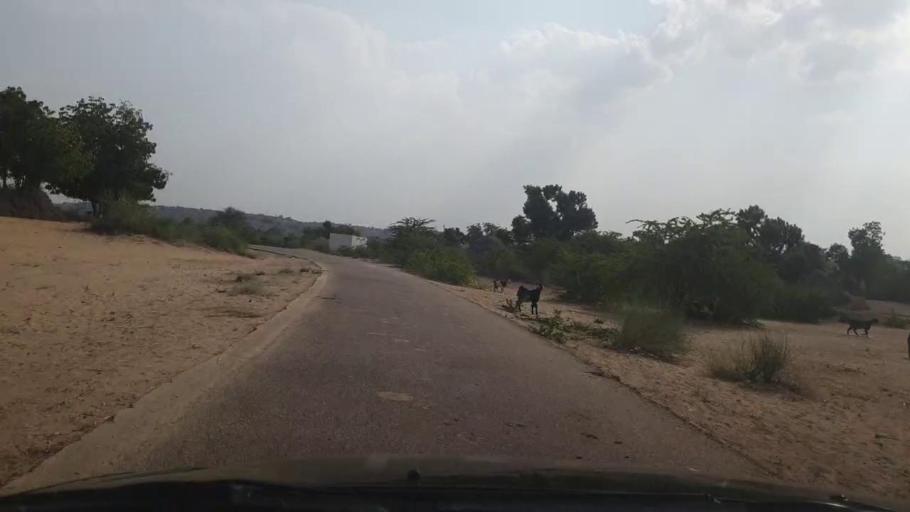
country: PK
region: Sindh
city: Islamkot
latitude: 25.0150
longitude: 70.5926
